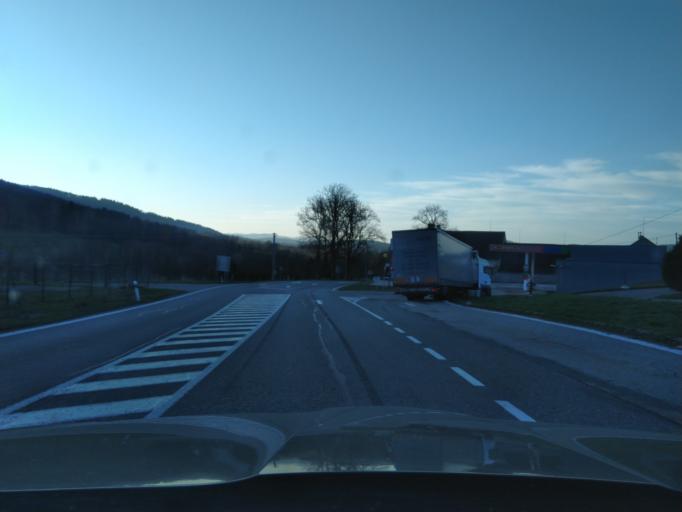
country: CZ
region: Jihocesky
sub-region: Okres Prachatice
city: Borova Lada
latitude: 48.9614
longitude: 13.7556
